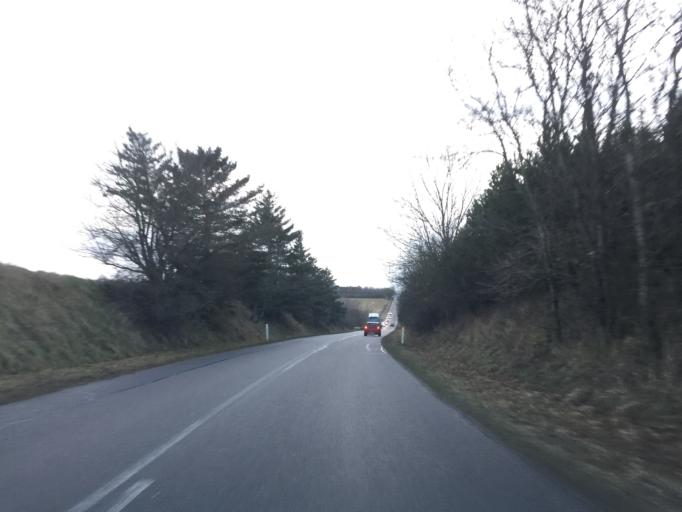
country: DK
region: Central Jutland
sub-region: Viborg Kommune
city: Bjerringbro
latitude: 56.3480
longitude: 9.6575
